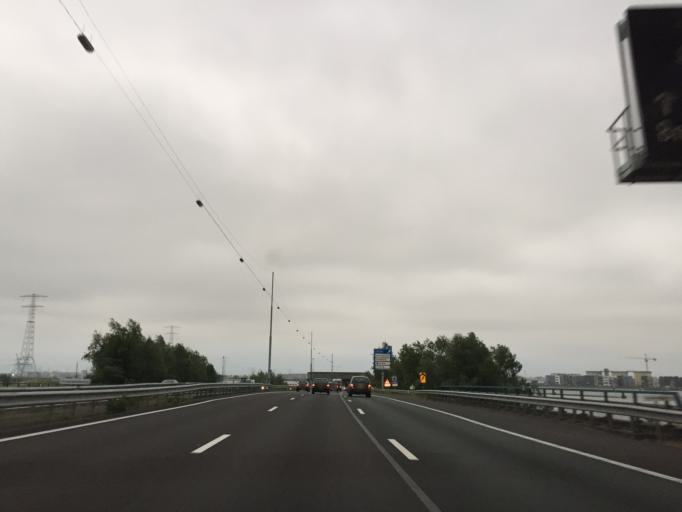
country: NL
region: North Holland
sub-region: Gemeente Diemen
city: Diemen
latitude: 52.3805
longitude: 4.9731
